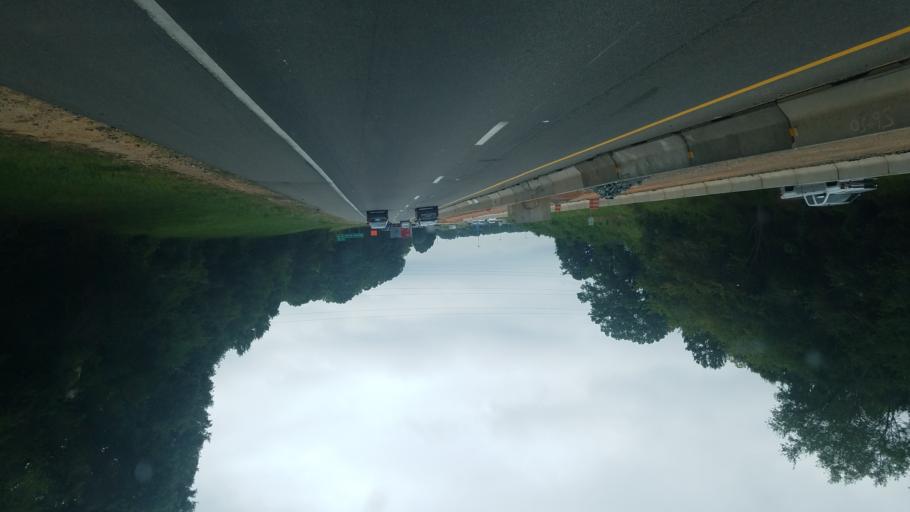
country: US
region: North Carolina
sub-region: Iredell County
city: Mooresville
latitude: 35.5719
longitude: -80.8563
